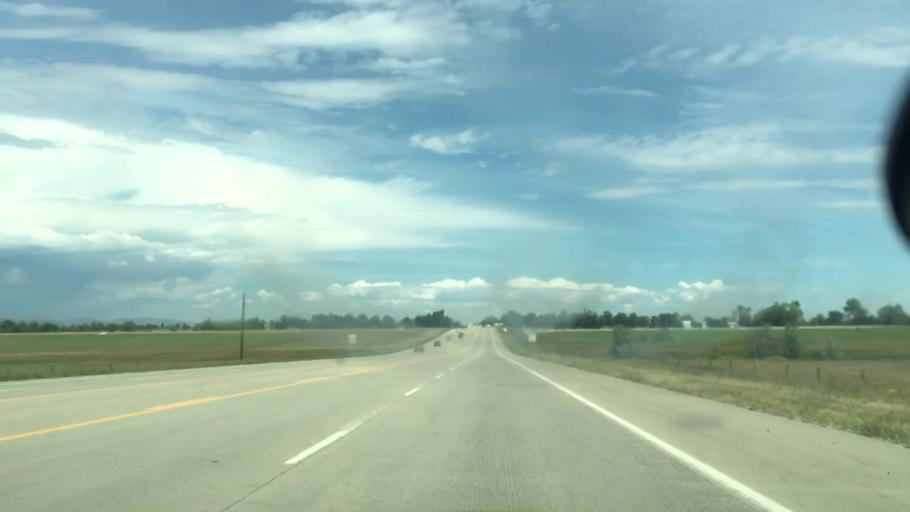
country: US
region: Colorado
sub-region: Boulder County
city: Longmont
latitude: 40.2262
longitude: -105.1023
